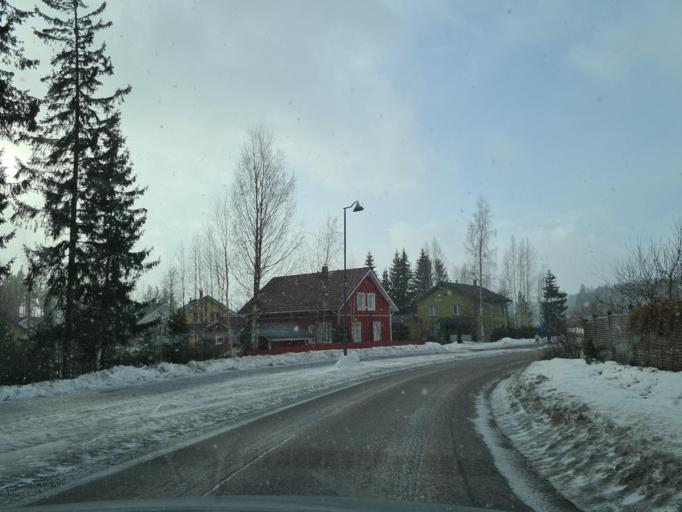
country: FI
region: Uusimaa
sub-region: Helsinki
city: Maentsaelae
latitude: 60.6540
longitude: 25.3093
